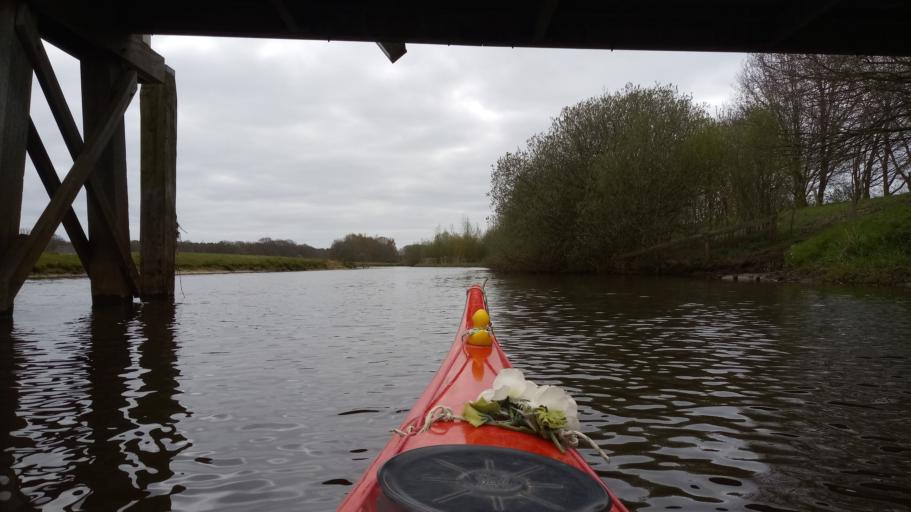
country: NL
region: Overijssel
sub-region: Gemeente Twenterand
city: Den Ham
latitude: 52.4986
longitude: 6.4134
